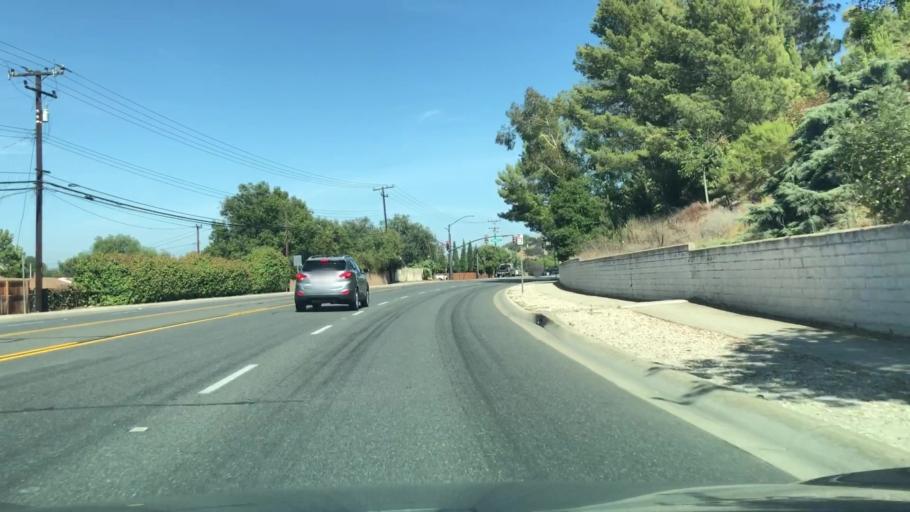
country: US
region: California
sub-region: Ventura County
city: Casa Conejo
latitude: 34.1796
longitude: -118.9457
